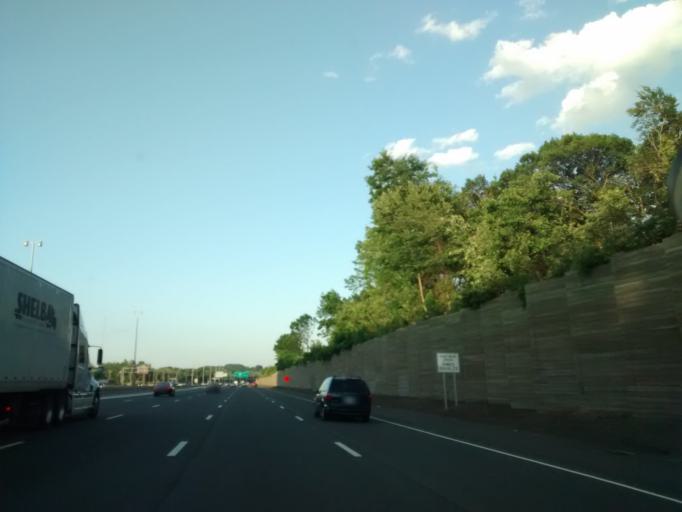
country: US
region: Connecticut
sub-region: Hartford County
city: East Hartford
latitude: 41.7679
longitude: -72.6166
